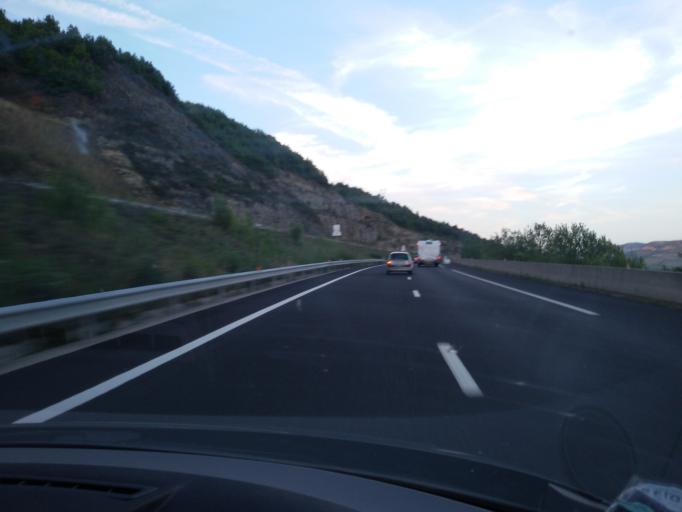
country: FR
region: Languedoc-Roussillon
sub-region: Departement de la Lozere
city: Chirac
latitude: 44.4924
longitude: 3.2232
